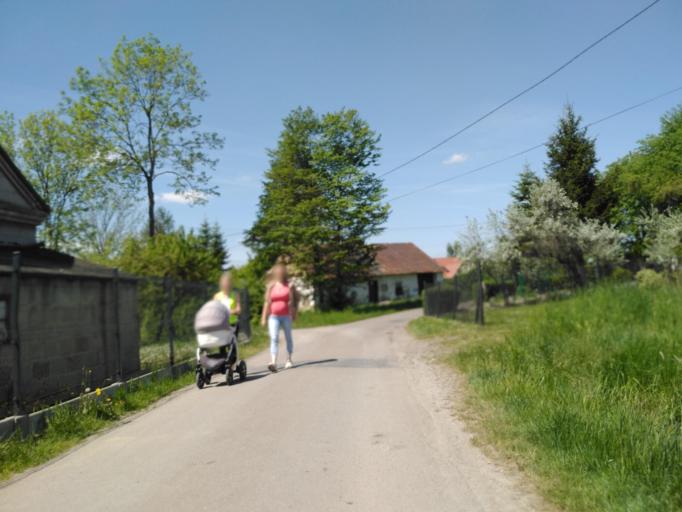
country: PL
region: Subcarpathian Voivodeship
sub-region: Powiat krosnienski
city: Chorkowka
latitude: 49.6766
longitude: 21.6956
